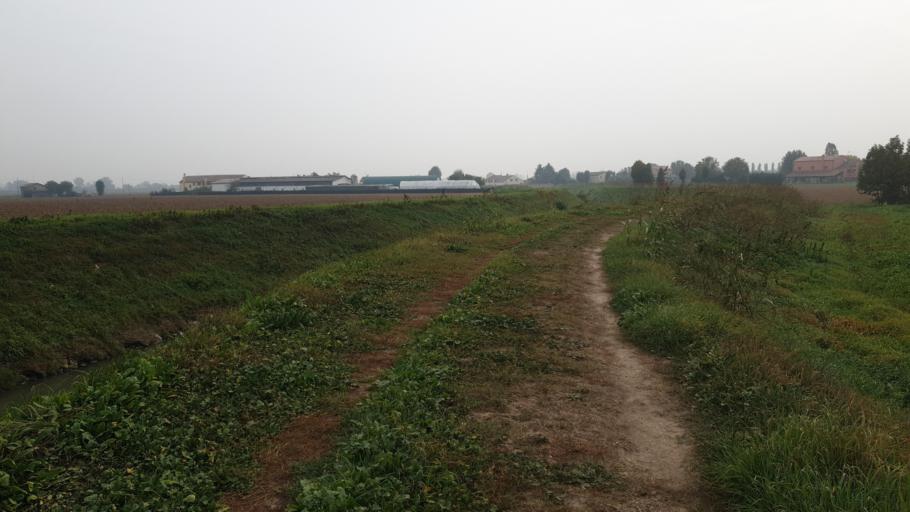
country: IT
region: Veneto
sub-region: Provincia di Padova
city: Casalserugo
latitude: 45.3337
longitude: 11.9263
